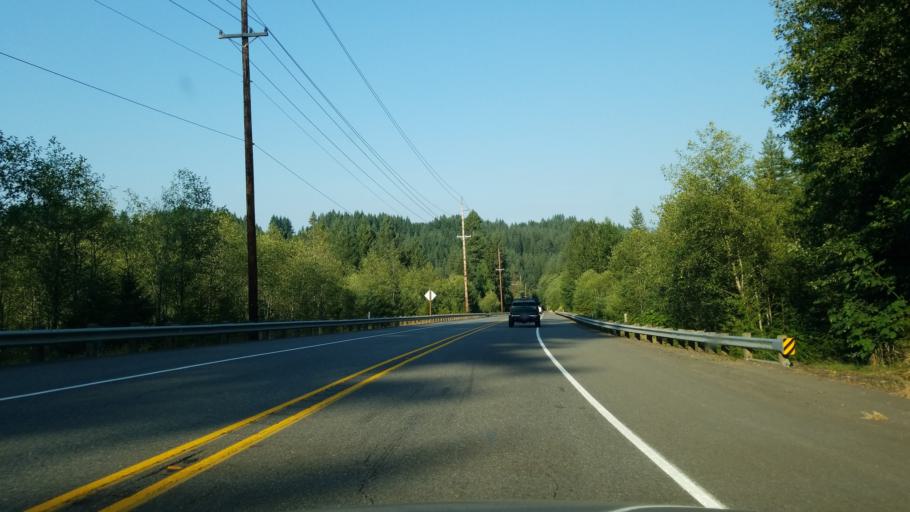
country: US
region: Oregon
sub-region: Clackamas County
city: Estacada
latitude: 45.2234
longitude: -122.3622
